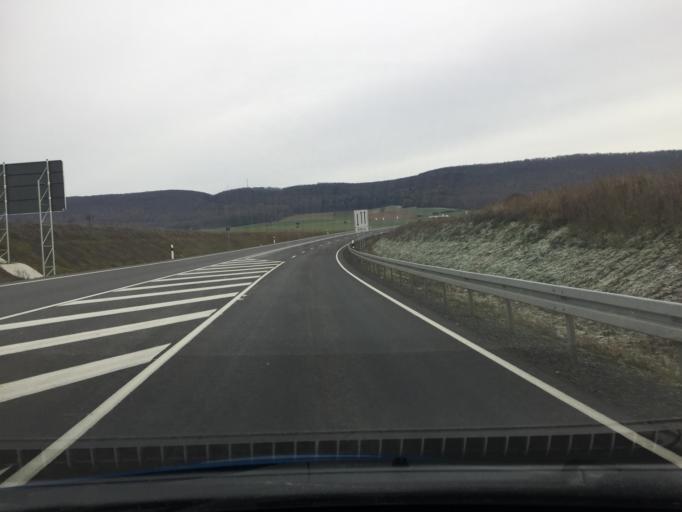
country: DE
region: Lower Saxony
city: Luerdissen
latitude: 51.9445
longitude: 9.6305
